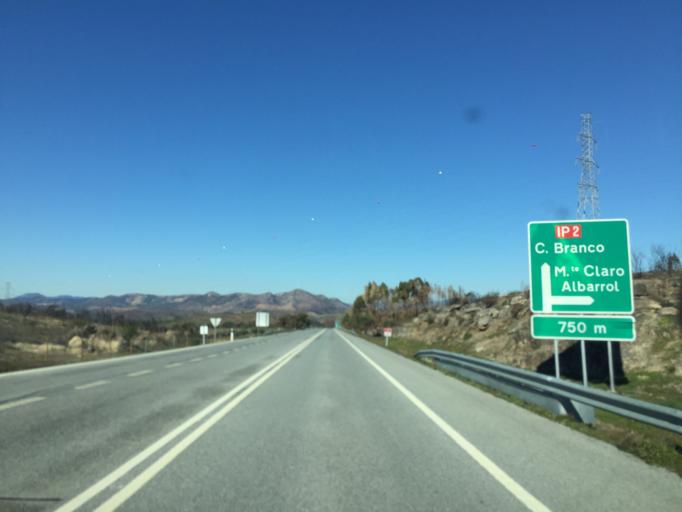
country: PT
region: Portalegre
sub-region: Nisa
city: Nisa
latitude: 39.5239
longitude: -7.7829
